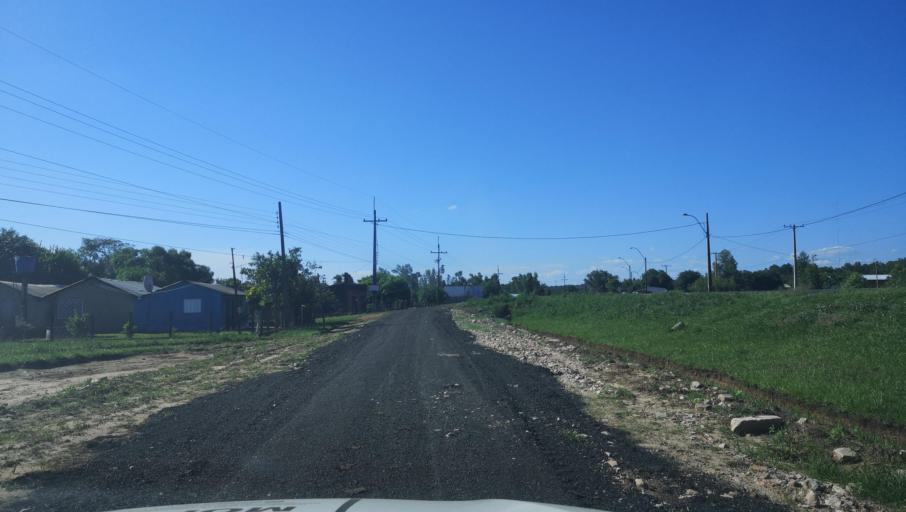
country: PY
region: Caaguazu
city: Carayao
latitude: -25.2034
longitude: -56.3994
